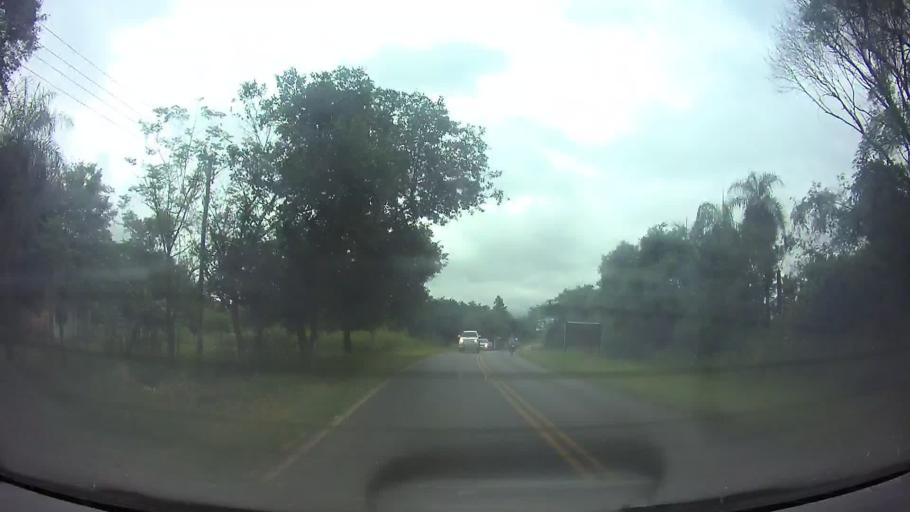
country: PY
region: Central
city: Guarambare
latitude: -25.5284
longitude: -57.4976
